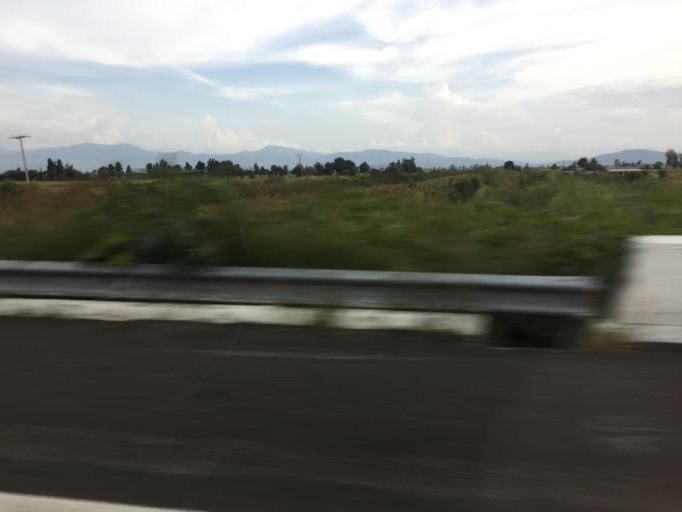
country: MX
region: Michoacan
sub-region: Alvaro Obregon
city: Lazaro Cardenas (La Purisima)
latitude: 19.8915
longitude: -101.0056
